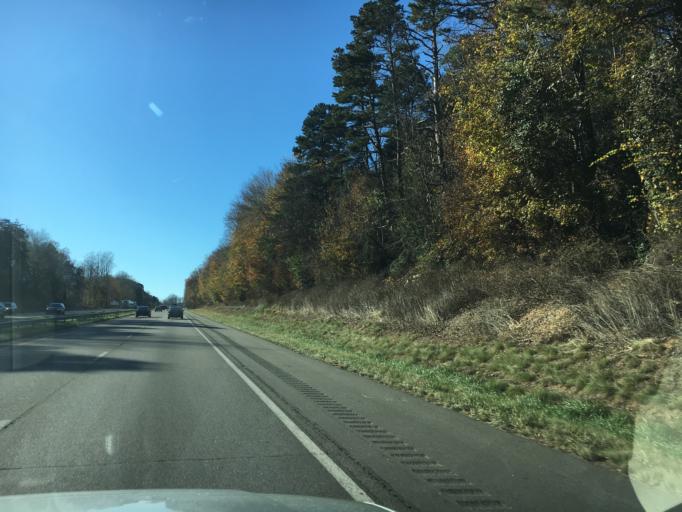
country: US
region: North Carolina
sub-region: Catawba County
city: Claremont
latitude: 35.7220
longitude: -81.1644
